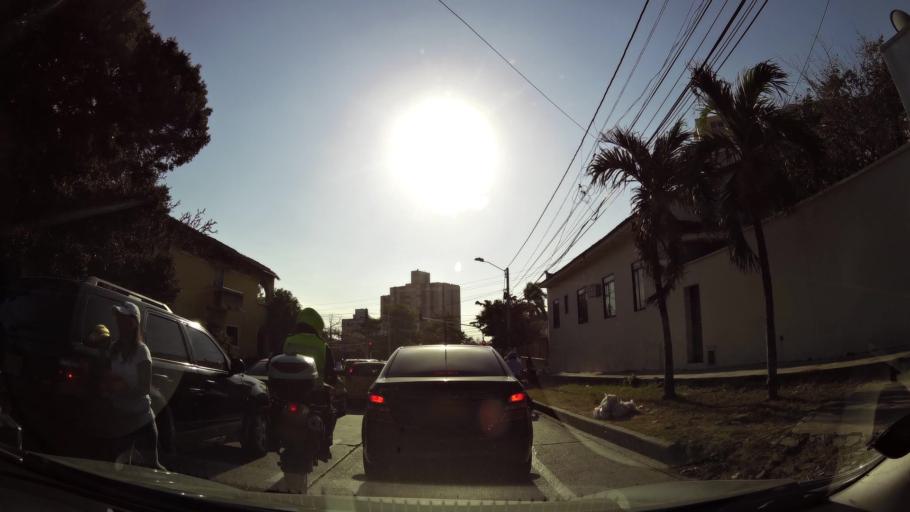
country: CO
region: Atlantico
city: Barranquilla
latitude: 10.9953
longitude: -74.8003
